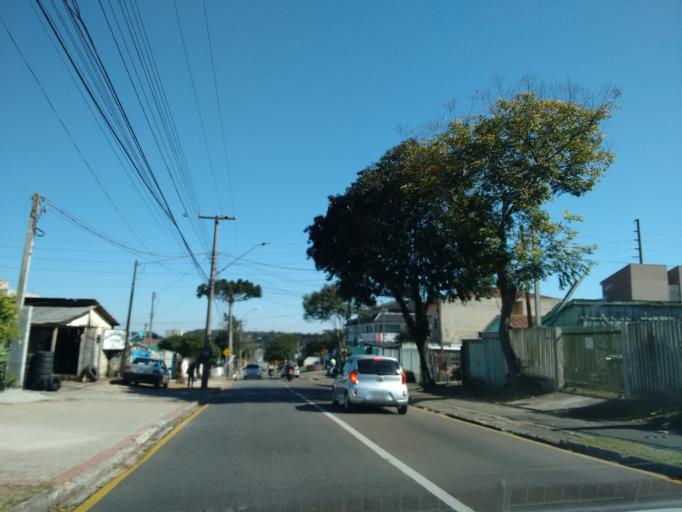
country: BR
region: Parana
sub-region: Curitiba
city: Curitiba
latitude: -25.5121
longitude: -49.3038
